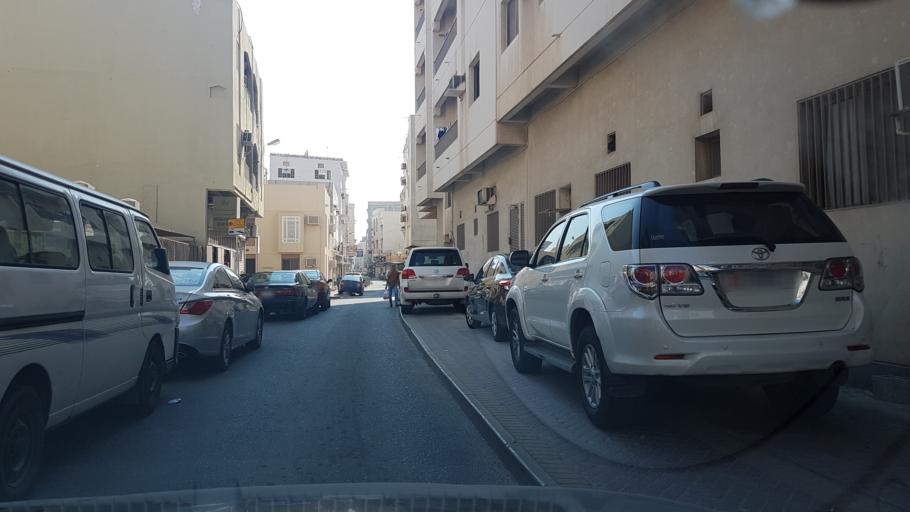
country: BH
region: Manama
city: Manama
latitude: 26.2340
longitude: 50.5801
